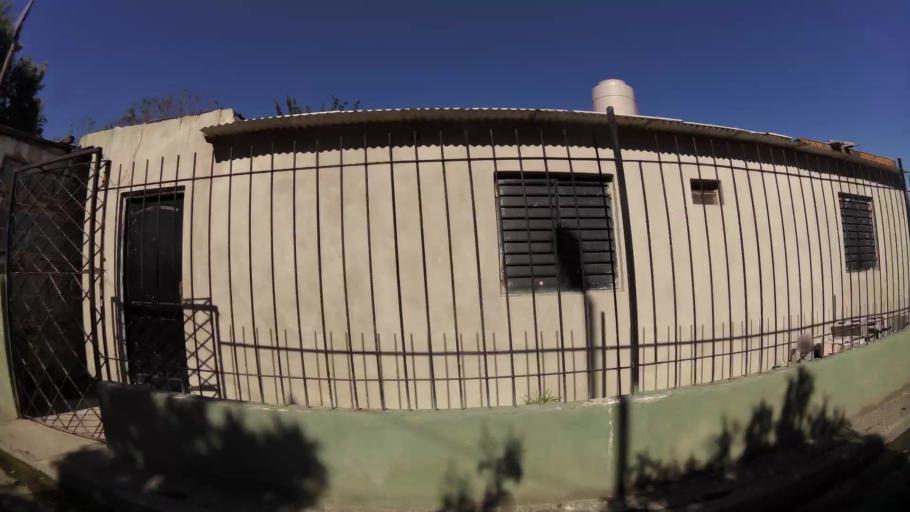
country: AR
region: Cordoba
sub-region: Departamento de Capital
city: Cordoba
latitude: -31.4036
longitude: -64.1505
